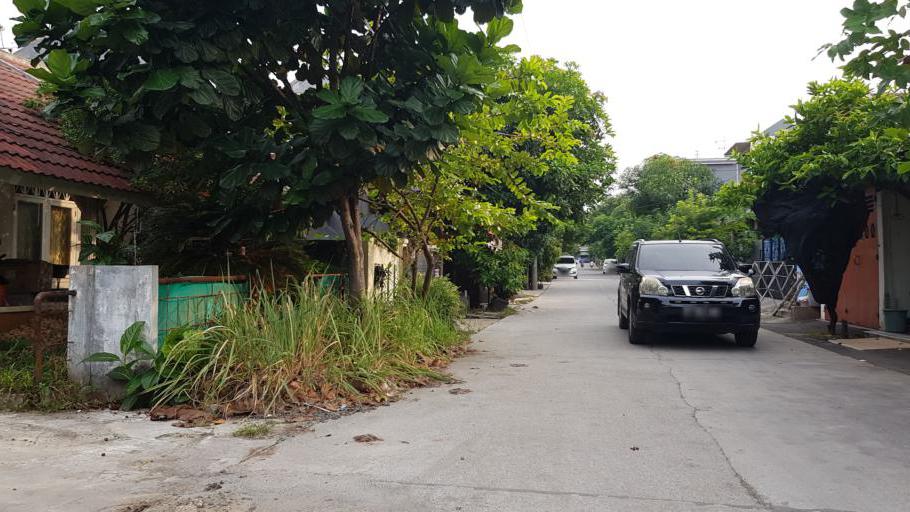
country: ID
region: West Java
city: Depok
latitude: -6.3711
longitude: 106.7953
